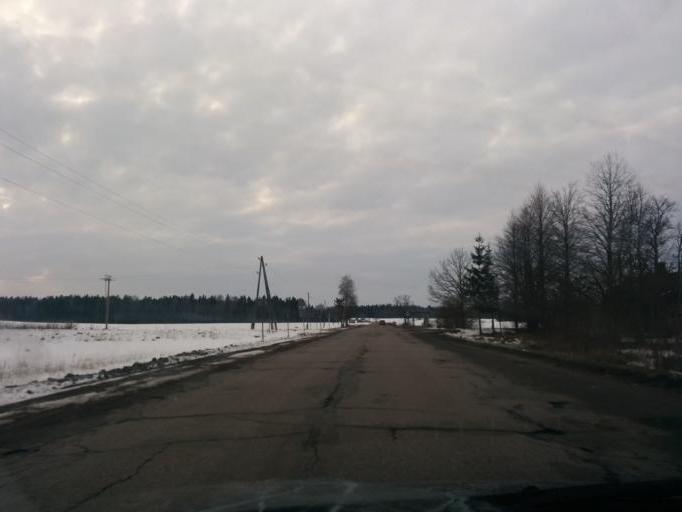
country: LV
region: Gulbenes Rajons
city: Gulbene
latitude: 57.1915
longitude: 26.9099
